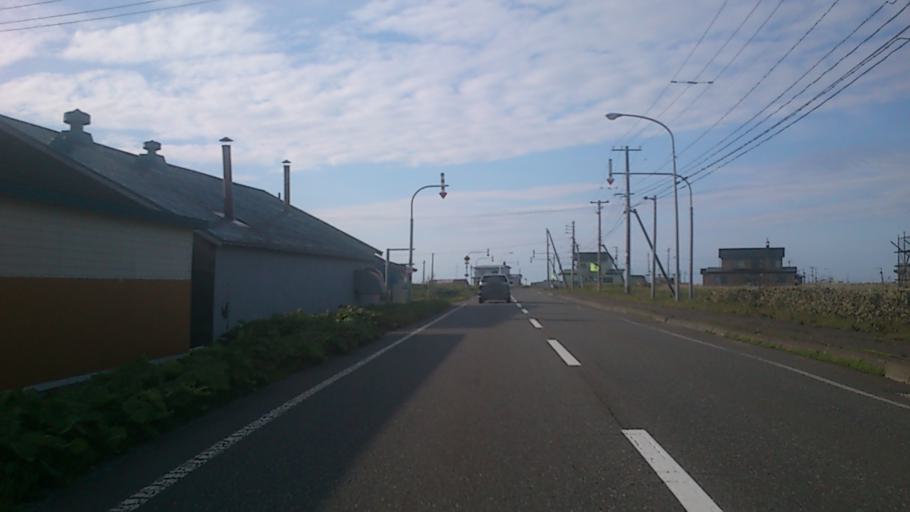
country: JP
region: Hokkaido
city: Wakkanai
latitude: 45.4275
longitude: 141.6383
